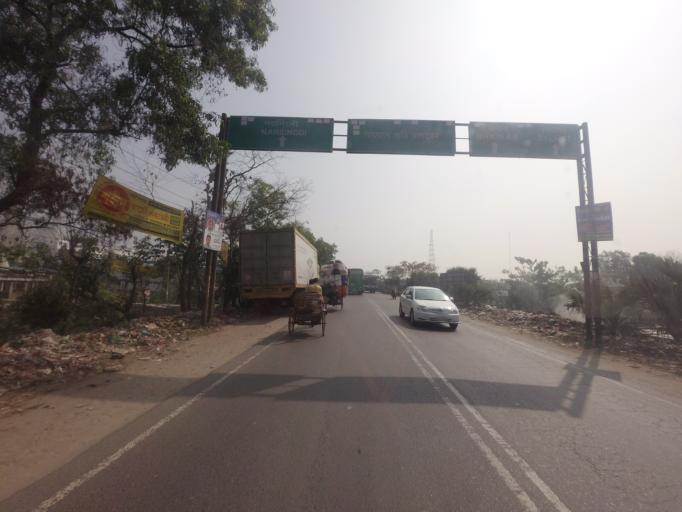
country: BD
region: Dhaka
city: Narsingdi
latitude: 23.8935
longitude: 90.6662
